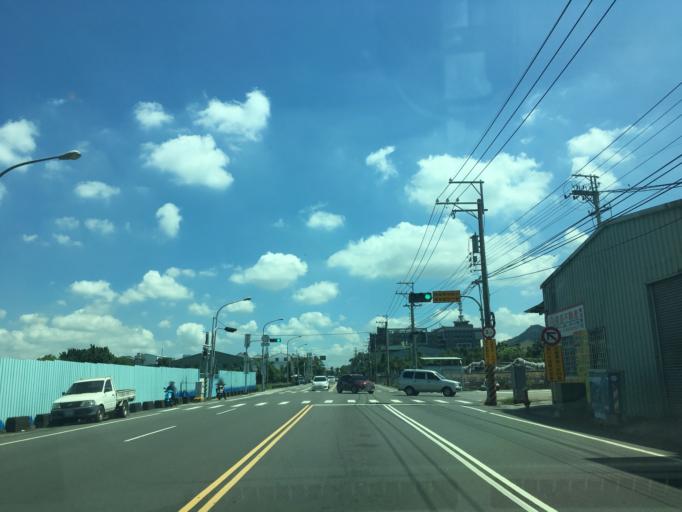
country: TW
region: Taiwan
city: Fengyuan
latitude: 24.1975
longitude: 120.7217
